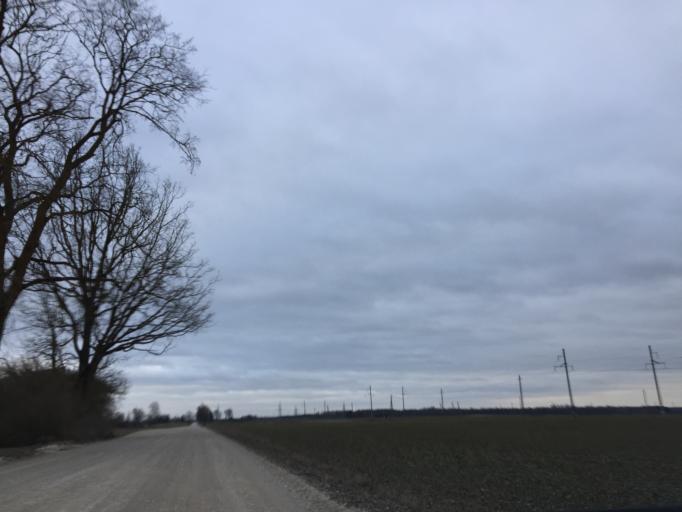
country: LT
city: Zagare
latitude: 56.3445
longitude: 23.2510
